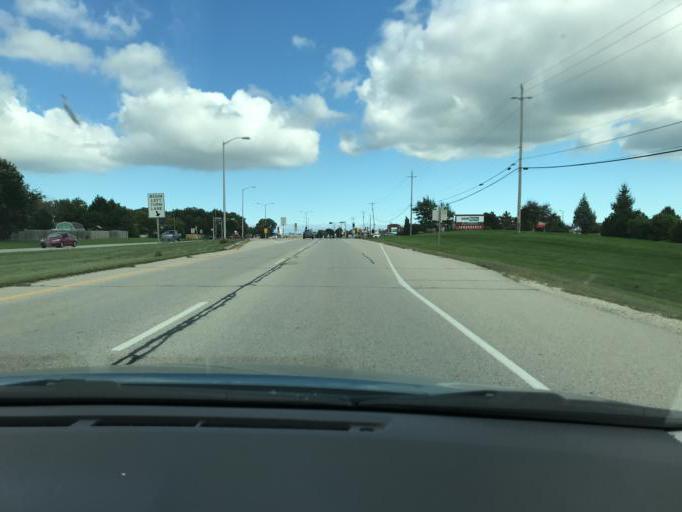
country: US
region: Wisconsin
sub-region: Kenosha County
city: Pleasant Prairie
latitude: 42.5667
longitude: -87.9242
